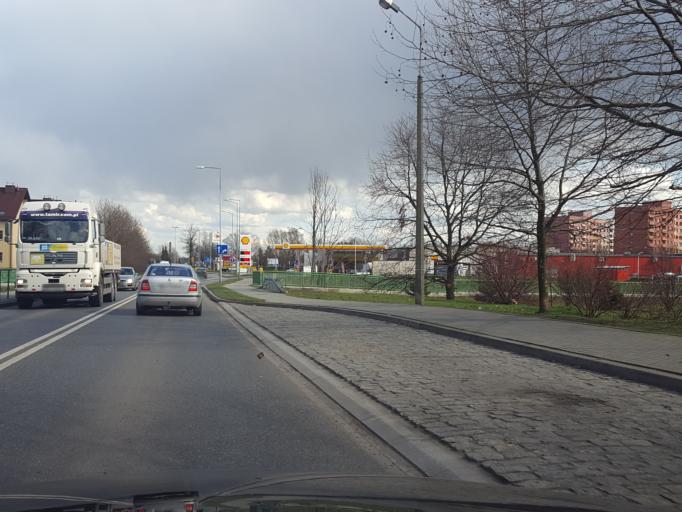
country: PL
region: Silesian Voivodeship
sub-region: Powiat pszczynski
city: Pszczyna
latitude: 49.9708
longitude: 18.9431
